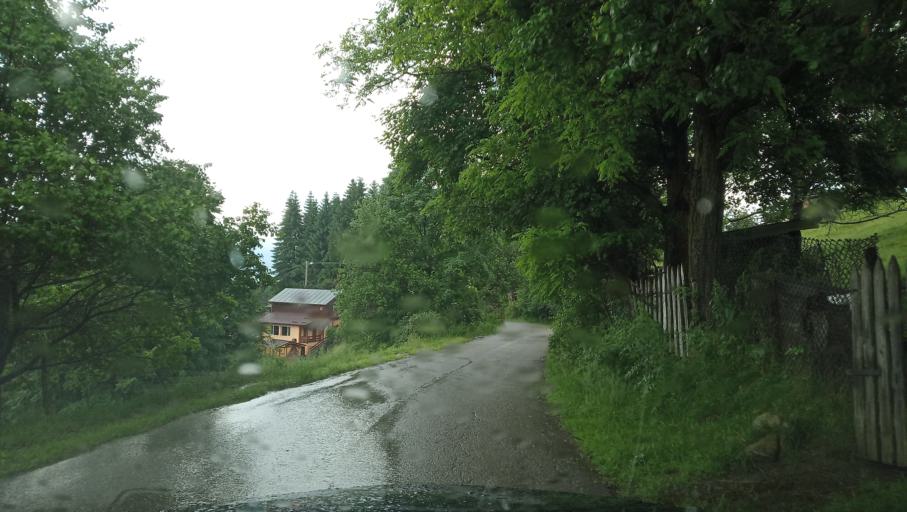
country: RO
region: Hunedoara
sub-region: Oras Petrila
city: Petrila
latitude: 45.3906
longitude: 23.4368
